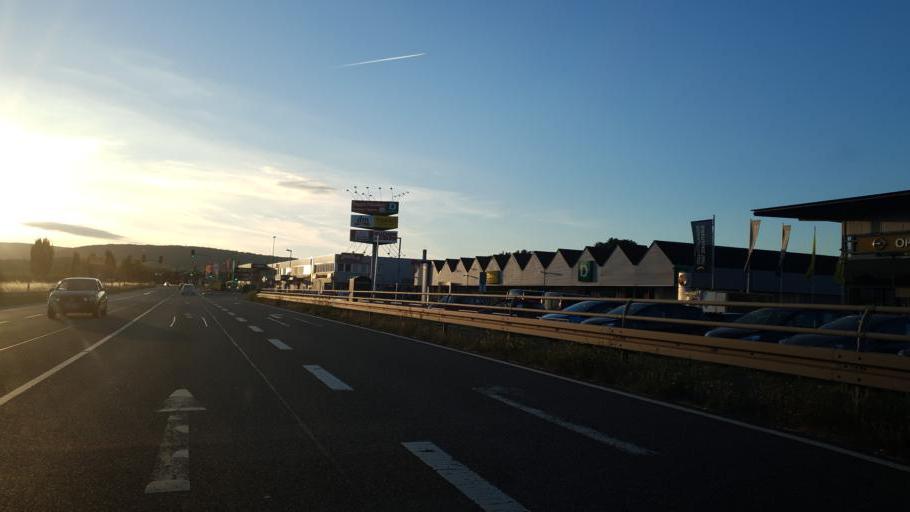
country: DE
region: Hesse
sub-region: Regierungsbezirk Darmstadt
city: Hattersheim
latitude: 50.0754
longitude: 8.4729
